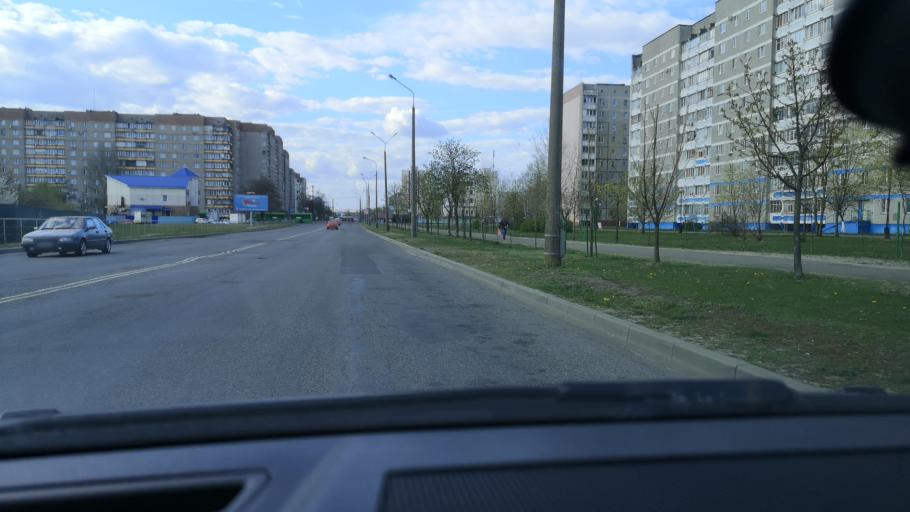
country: BY
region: Gomel
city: Gomel
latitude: 52.4010
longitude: 30.9220
